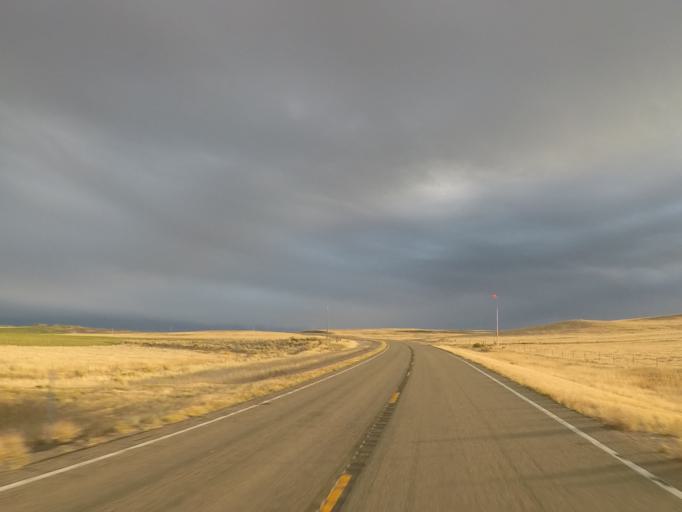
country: US
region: Montana
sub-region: Golden Valley County
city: Ryegate
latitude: 46.3604
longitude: -109.2682
